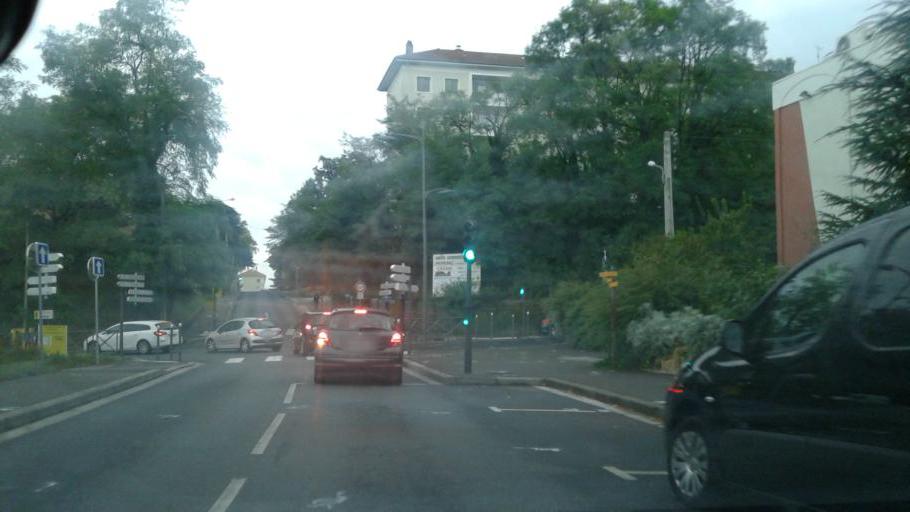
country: FR
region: Rhone-Alpes
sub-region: Departement du Rhone
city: Rillieux-la-Pape
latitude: 45.8234
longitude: 4.8958
